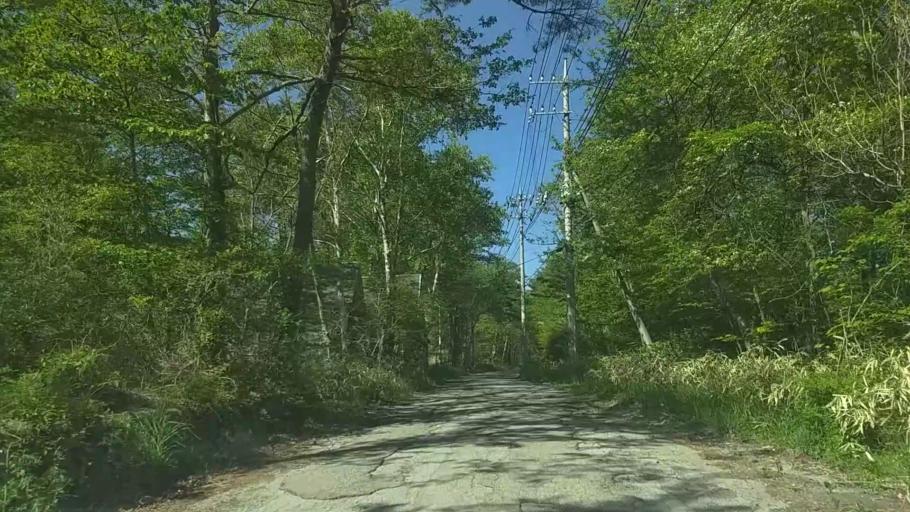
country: JP
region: Yamanashi
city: Nirasaki
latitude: 35.9133
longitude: 138.4309
